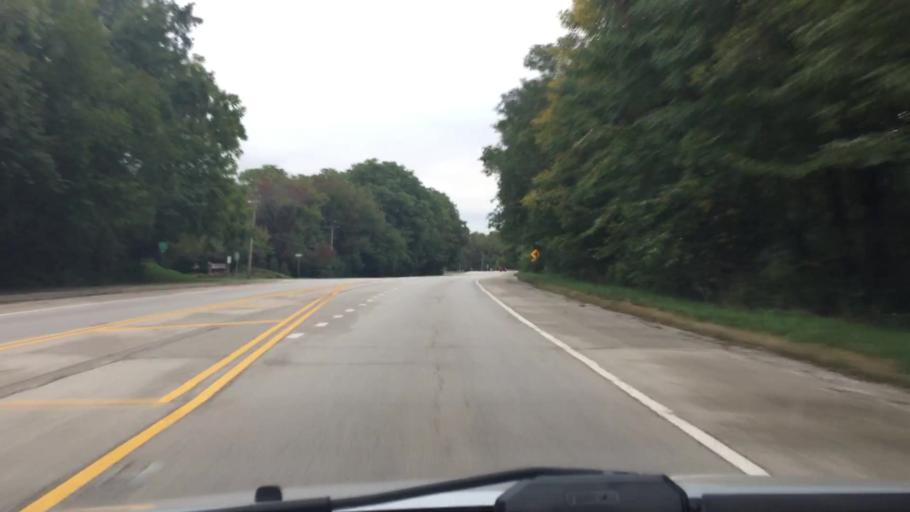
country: US
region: Illinois
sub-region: Kane County
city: Saint Charles
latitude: 41.9203
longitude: -88.3205
